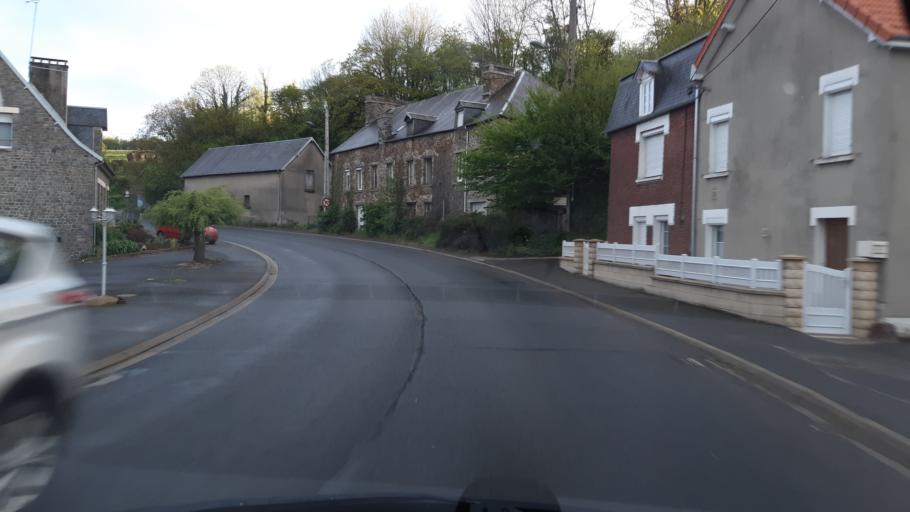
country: FR
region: Lower Normandy
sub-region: Departement de la Manche
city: Agneaux
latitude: 49.0922
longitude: -1.1170
